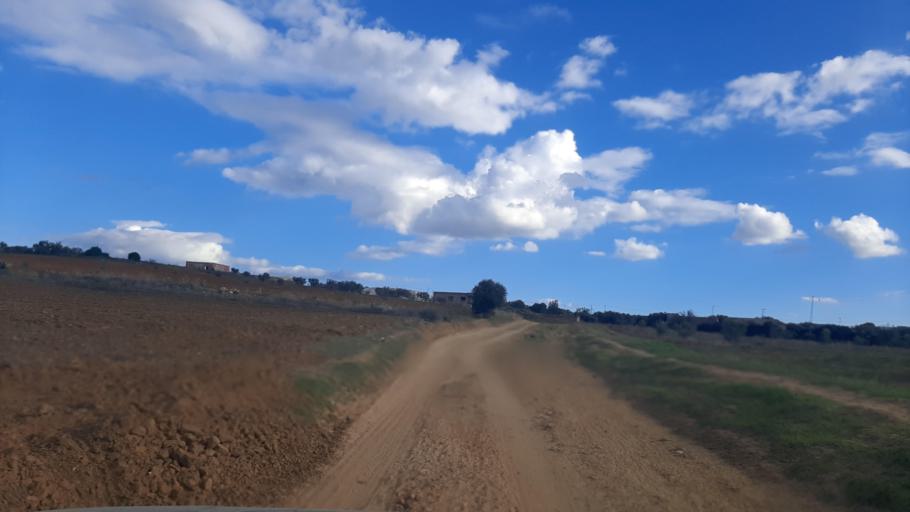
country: TN
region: Nabul
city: Bu `Urqub
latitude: 36.4446
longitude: 10.5047
